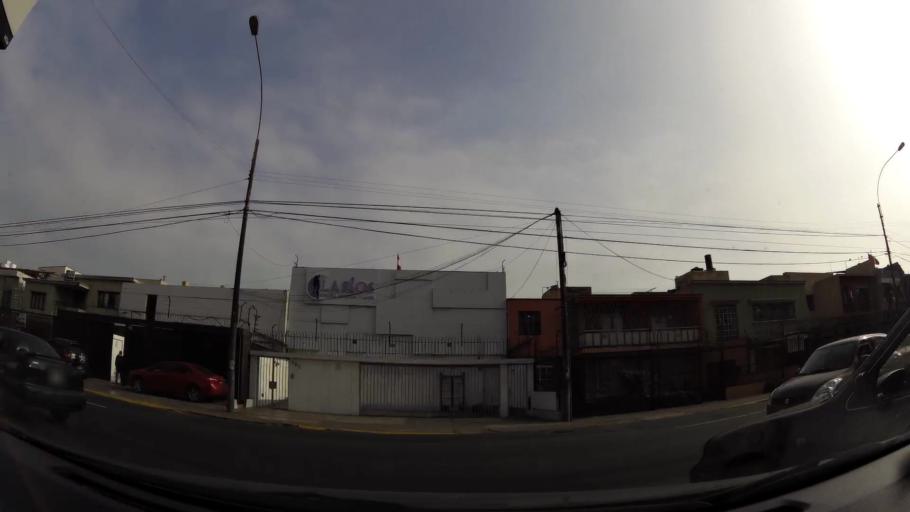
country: PE
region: Lima
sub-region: Lima
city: San Isidro
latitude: -12.0888
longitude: -77.0597
